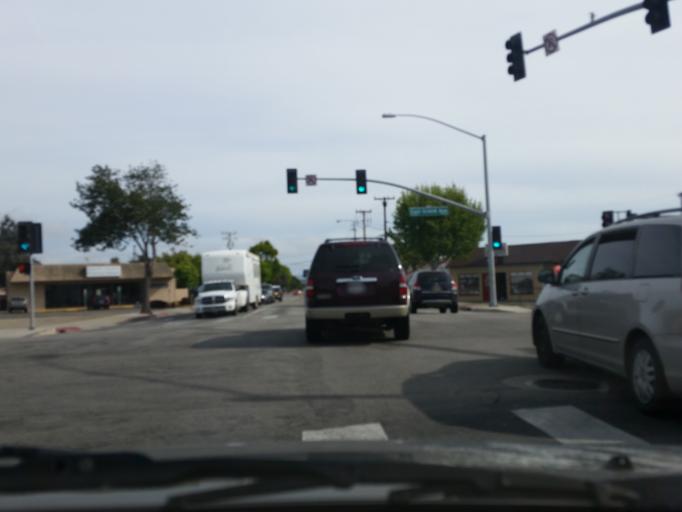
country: US
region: California
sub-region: San Luis Obispo County
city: Arroyo Grande
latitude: 35.1189
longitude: -120.5916
